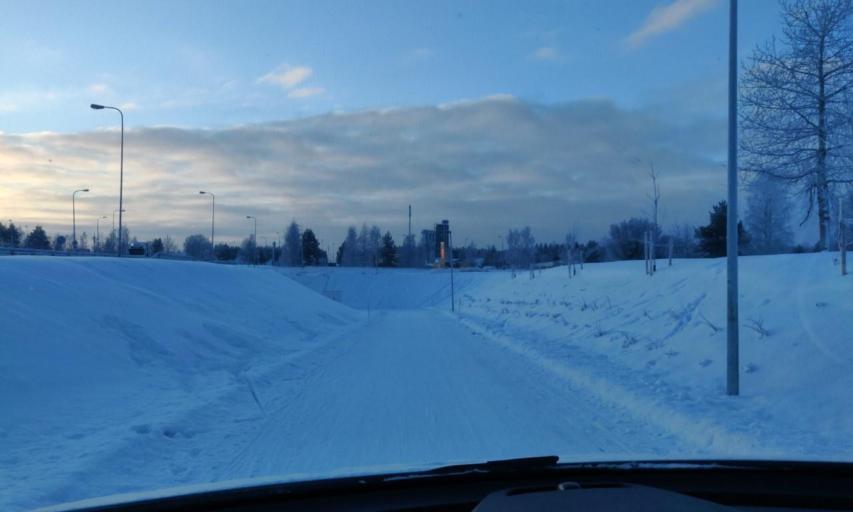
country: FI
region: Northern Ostrobothnia
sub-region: Ylivieska
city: Ylivieska
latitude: 64.0741
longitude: 24.5127
